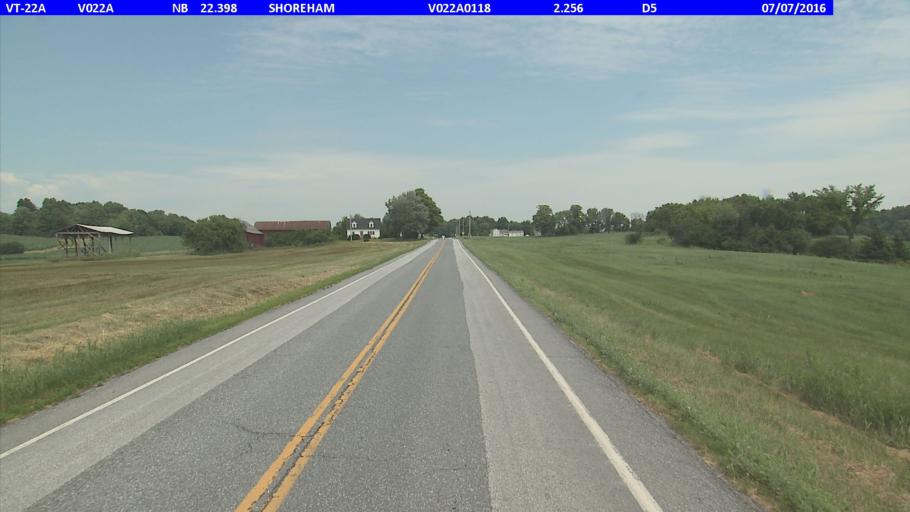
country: US
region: New York
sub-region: Essex County
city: Ticonderoga
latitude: 43.8820
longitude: -73.3096
